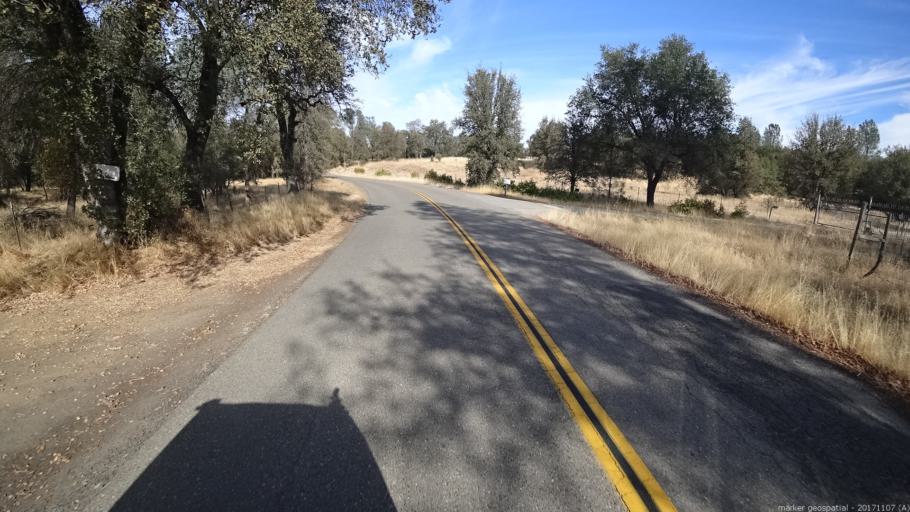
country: US
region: California
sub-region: Shasta County
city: Shasta
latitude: 40.4024
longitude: -122.5194
